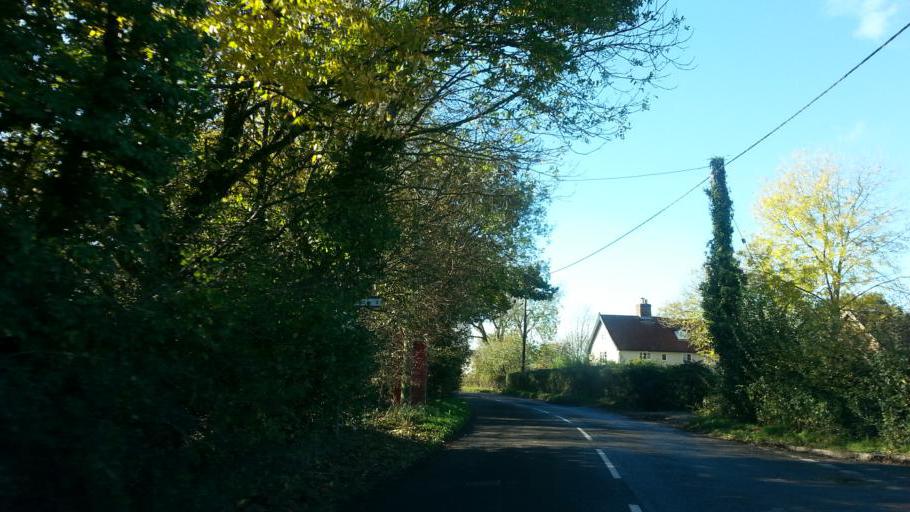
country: GB
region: England
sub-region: Suffolk
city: Cookley
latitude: 52.2964
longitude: 1.4037
